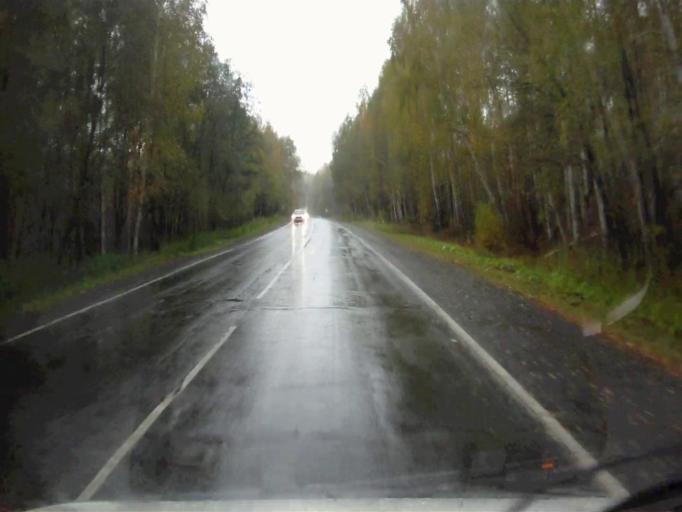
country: RU
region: Chelyabinsk
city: Kyshtym
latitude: 55.9091
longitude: 60.4372
